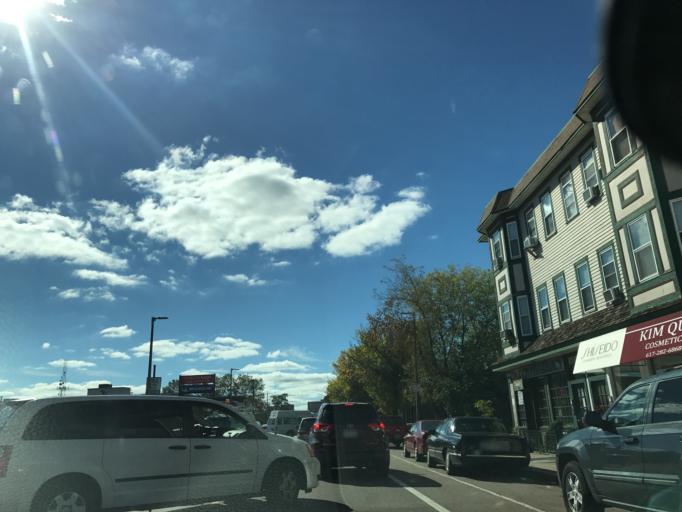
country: US
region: Massachusetts
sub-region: Suffolk County
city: South Boston
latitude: 42.3111
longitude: -71.0577
